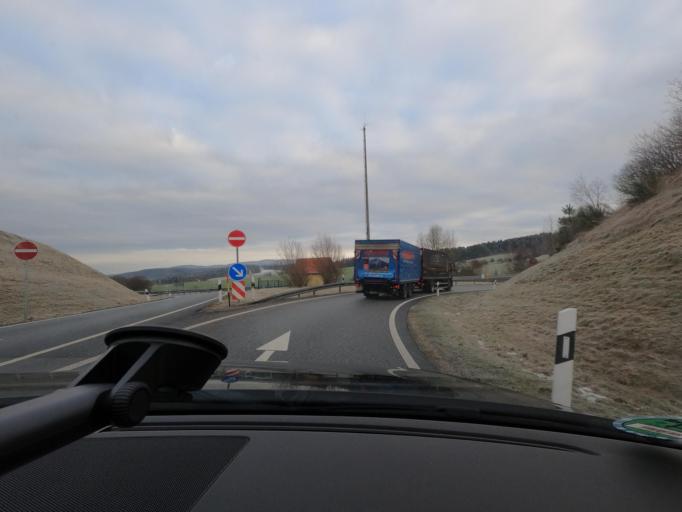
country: DE
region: Thuringia
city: Sankt Kilian
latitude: 50.5169
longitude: 10.7661
